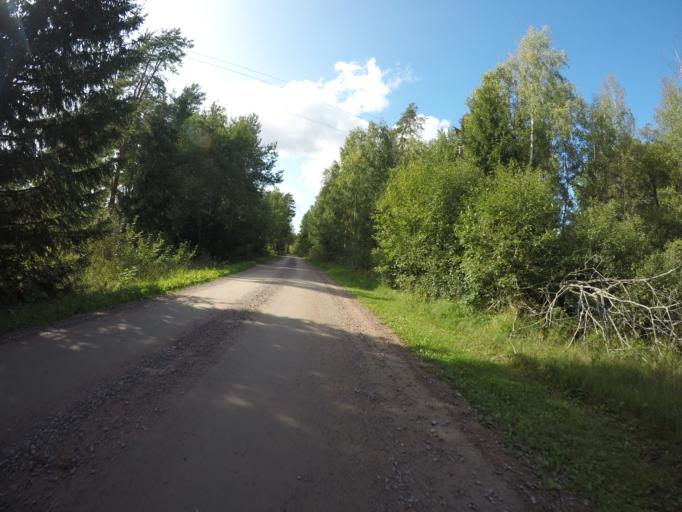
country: SE
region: Soedermanland
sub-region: Eskilstuna Kommun
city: Kvicksund
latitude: 59.5257
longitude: 16.3420
